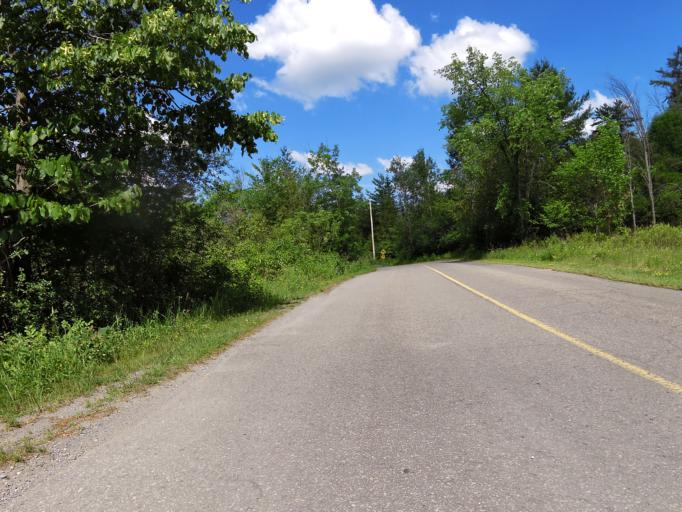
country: CA
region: Ontario
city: Arnprior
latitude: 45.4843
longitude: -76.2186
